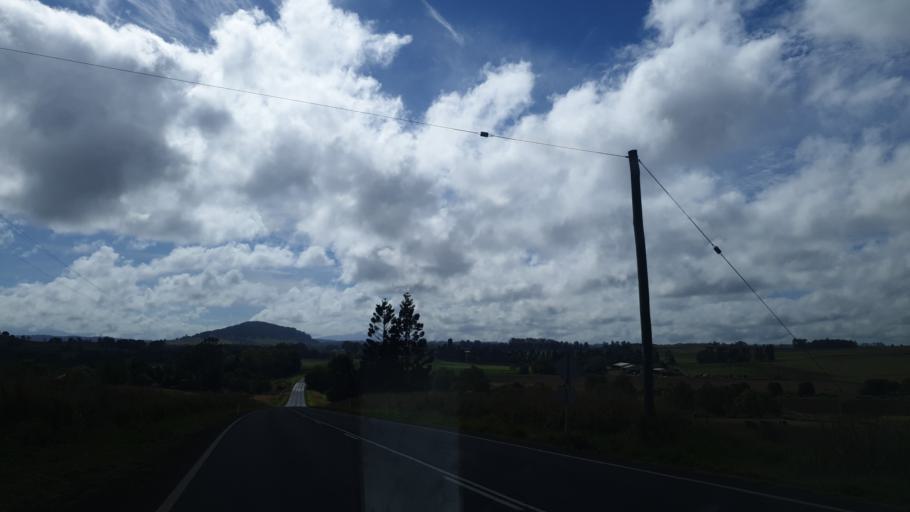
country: AU
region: Queensland
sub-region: Tablelands
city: Atherton
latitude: -17.2937
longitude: 145.5291
